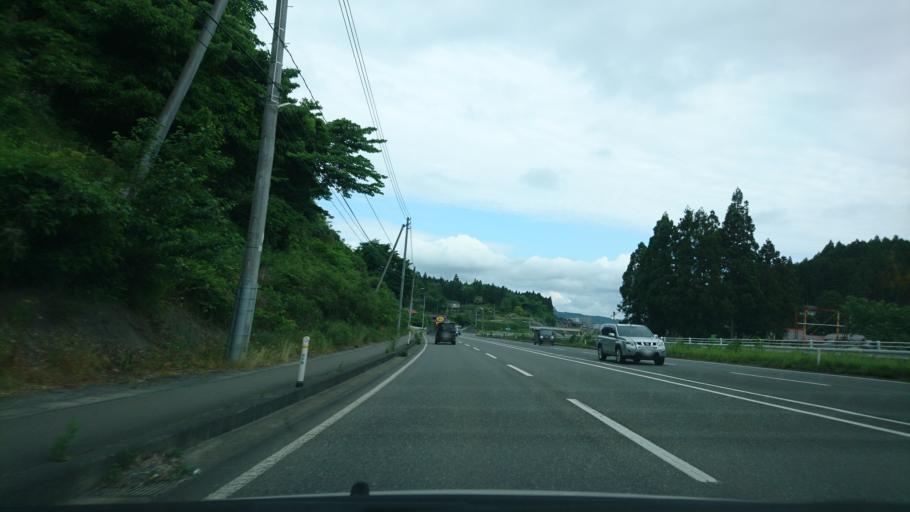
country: JP
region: Iwate
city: Ichinoseki
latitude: 38.9119
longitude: 141.1441
